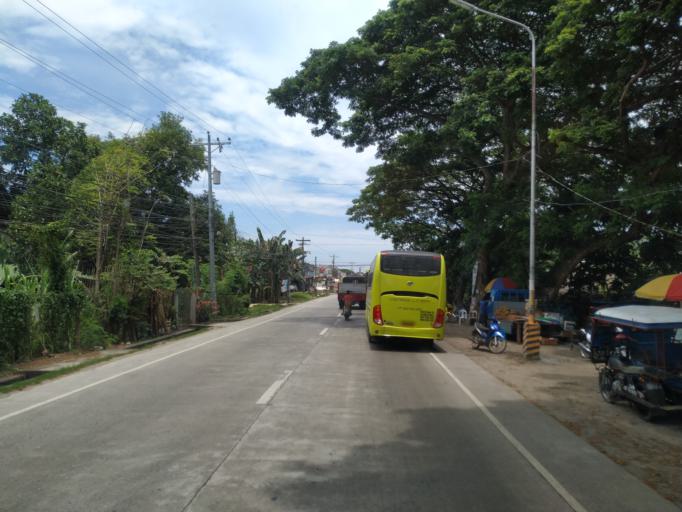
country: PH
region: Central Visayas
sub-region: Province of Negros Oriental
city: Sibulan
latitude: 9.3558
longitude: 123.2846
